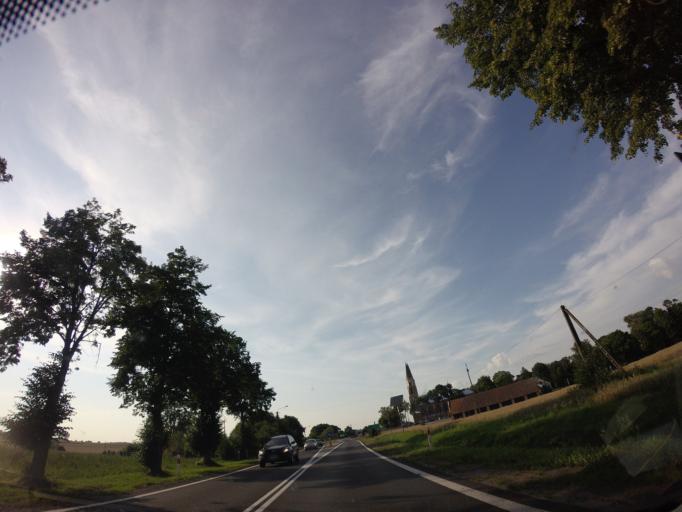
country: PL
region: Podlasie
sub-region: Powiat sokolski
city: Janow
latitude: 53.4385
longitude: 23.0967
